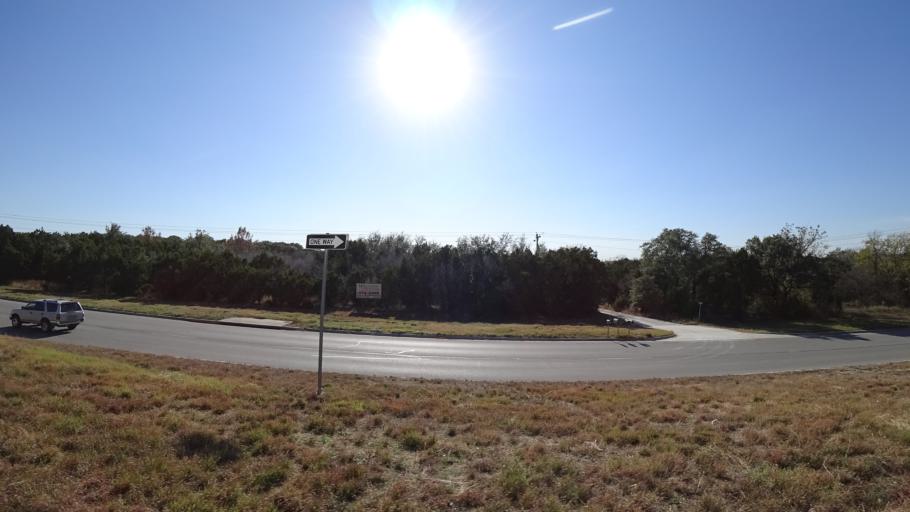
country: US
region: Texas
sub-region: Williamson County
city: Anderson Mill
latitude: 30.4585
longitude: -97.8357
